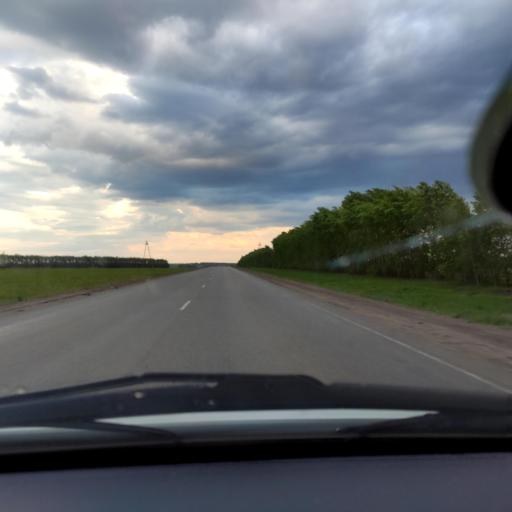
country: RU
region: Bashkortostan
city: Dyurtyuli
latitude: 55.3756
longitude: 54.8731
